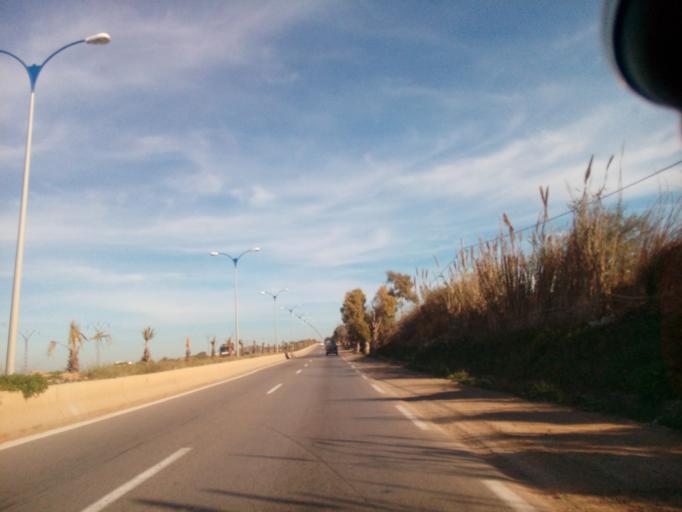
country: DZ
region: Mostaganem
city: Mostaganem
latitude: 35.8747
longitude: 0.0431
